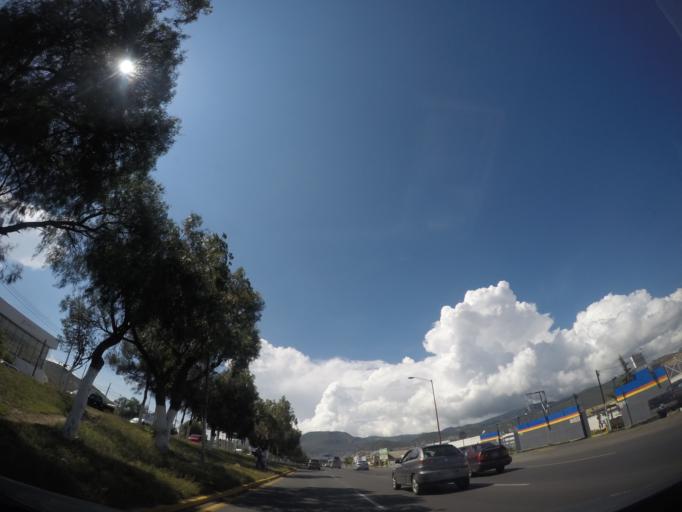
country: MX
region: Hidalgo
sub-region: Mineral de la Reforma
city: Unidad Minera 11 de Julio
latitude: 20.0993
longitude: -98.7168
